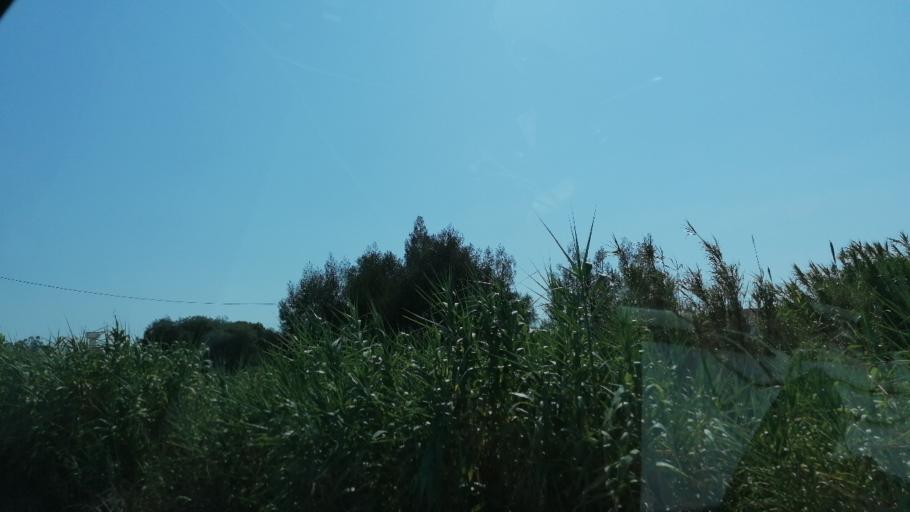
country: PT
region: Evora
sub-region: Vendas Novas
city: Vendas Novas
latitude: 38.6861
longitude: -8.6125
